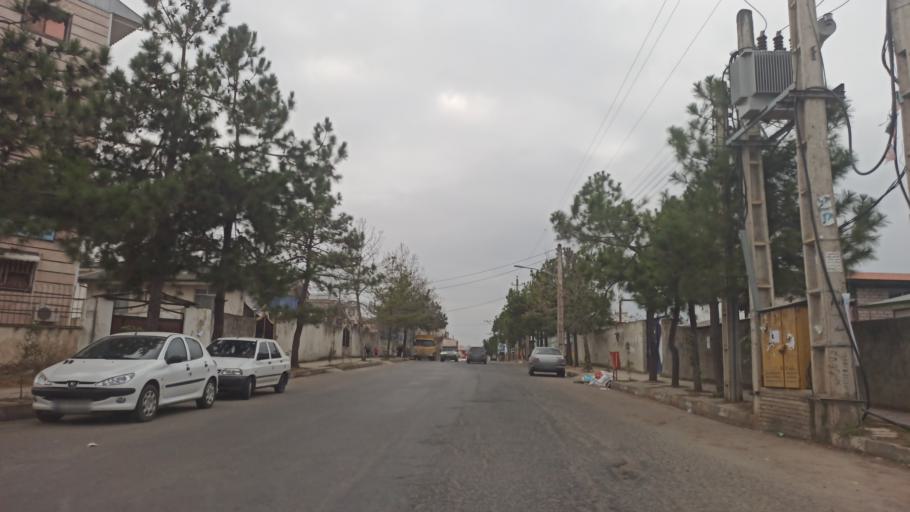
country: IR
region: Gilan
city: Fuman
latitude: 37.2309
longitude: 49.3125
